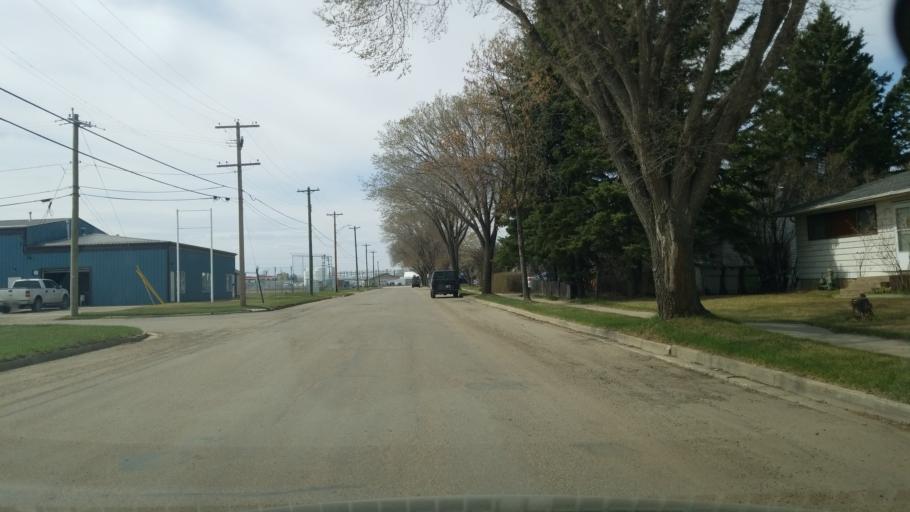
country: CA
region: Saskatchewan
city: Lloydminster
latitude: 53.2871
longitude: -110.0067
